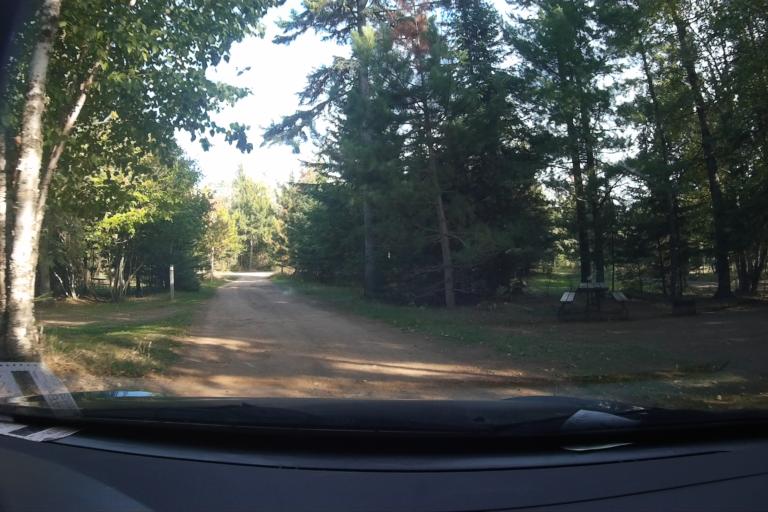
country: CA
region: Ontario
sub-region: Thunder Bay District
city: Thunder Bay
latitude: 48.3687
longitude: -88.8043
